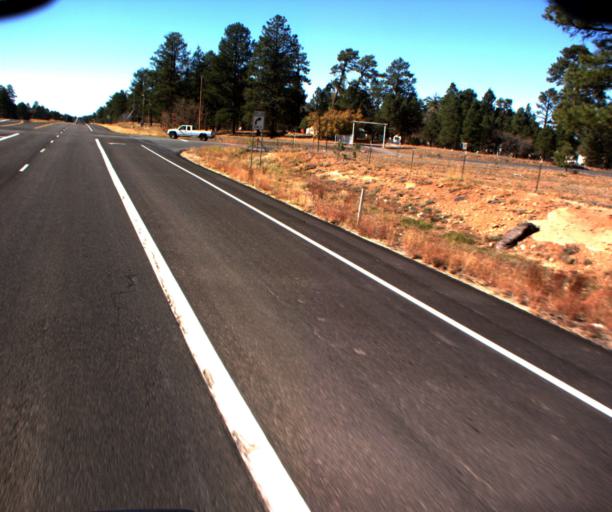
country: US
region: Arizona
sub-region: Apache County
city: Saint Michaels
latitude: 35.6787
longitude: -109.2037
